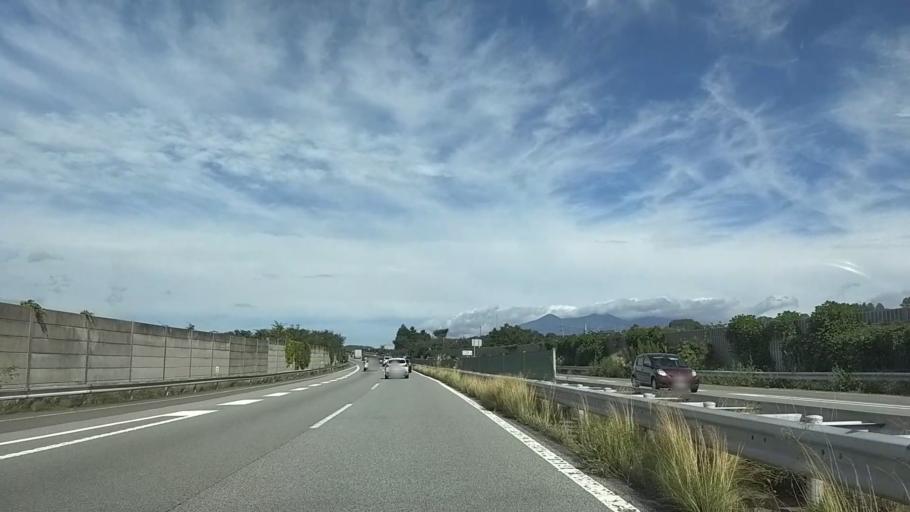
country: JP
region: Yamanashi
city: Nirasaki
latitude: 35.7542
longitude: 138.4401
